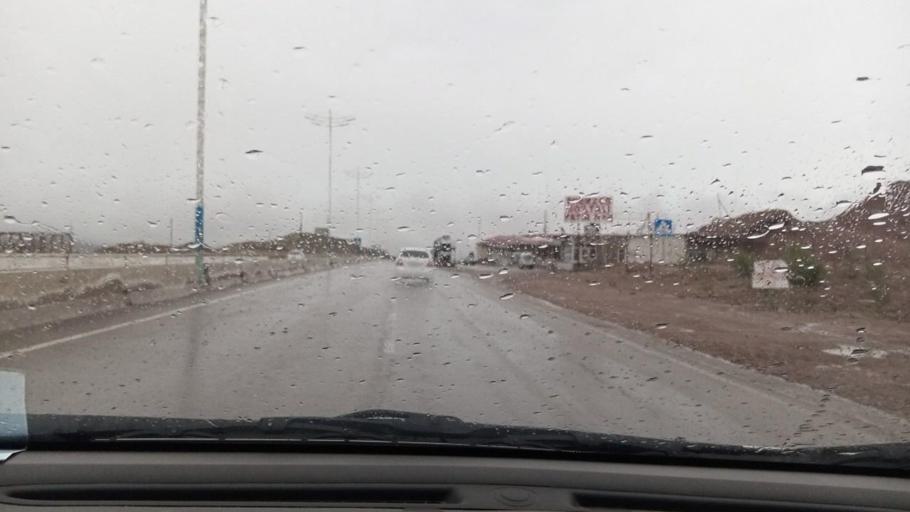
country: UZ
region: Namangan
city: Pop Shahri
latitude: 40.9216
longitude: 70.7365
